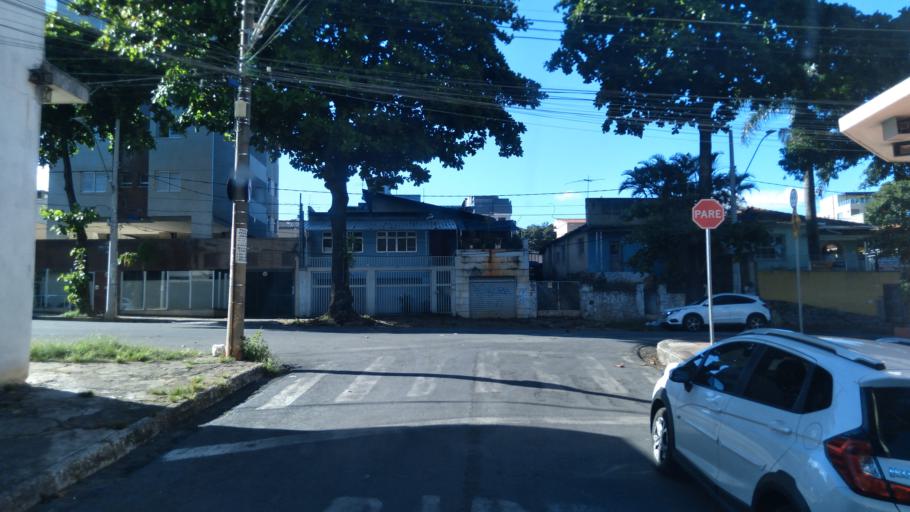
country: BR
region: Minas Gerais
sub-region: Belo Horizonte
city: Belo Horizonte
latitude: -19.9152
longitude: -43.9060
